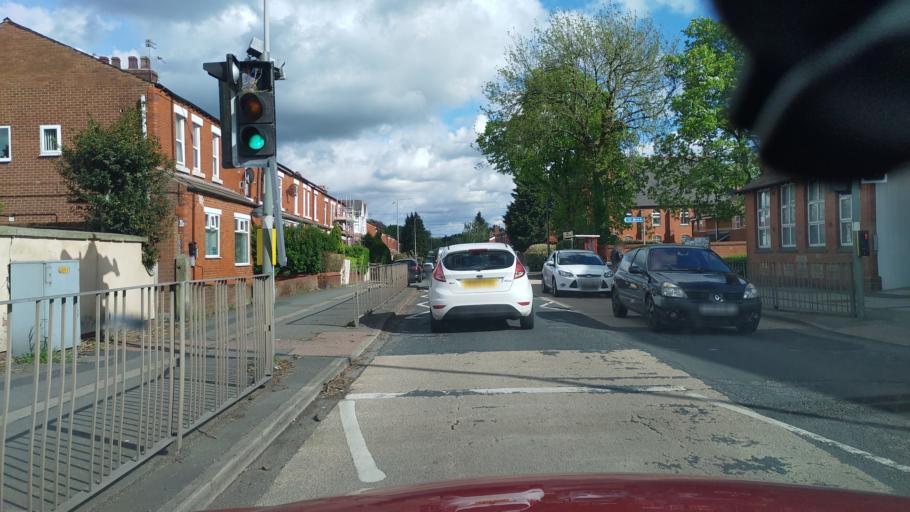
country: GB
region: England
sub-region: Lancashire
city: Leyland
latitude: 53.7222
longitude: -2.6863
